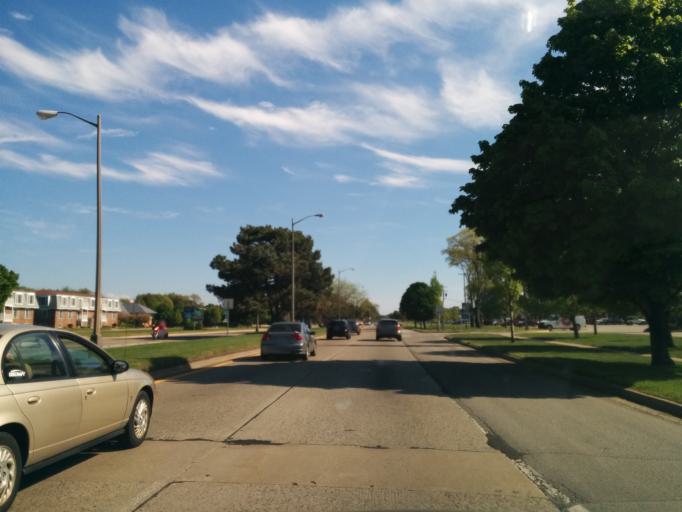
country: US
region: Michigan
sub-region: Ottawa County
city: Grand Haven
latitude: 43.0515
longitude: -86.2205
